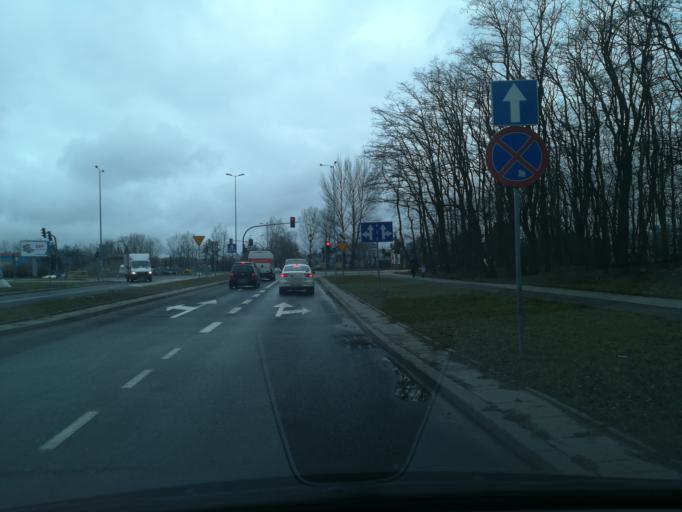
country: PL
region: Kujawsko-Pomorskie
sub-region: Powiat torunski
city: Lubicz Dolny
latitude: 53.0303
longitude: 18.7014
